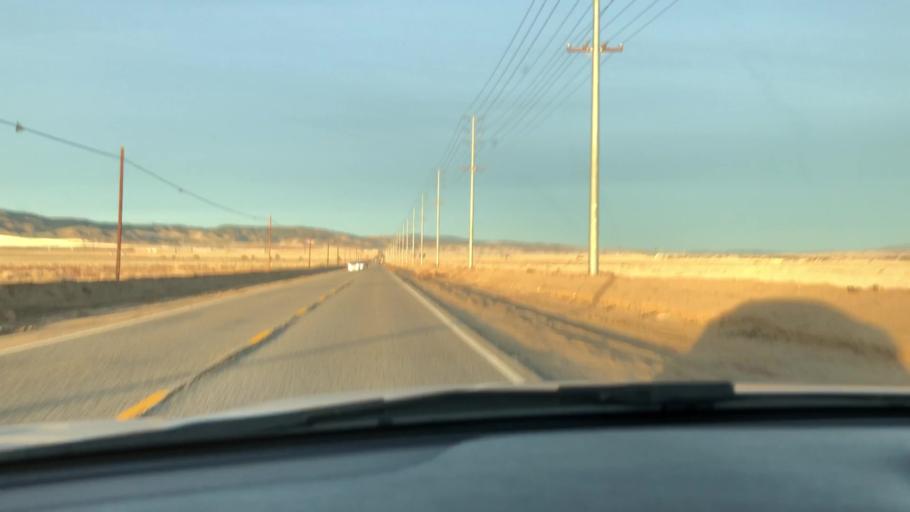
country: US
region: California
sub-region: Los Angeles County
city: Quartz Hill
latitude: 34.6747
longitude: -118.2567
